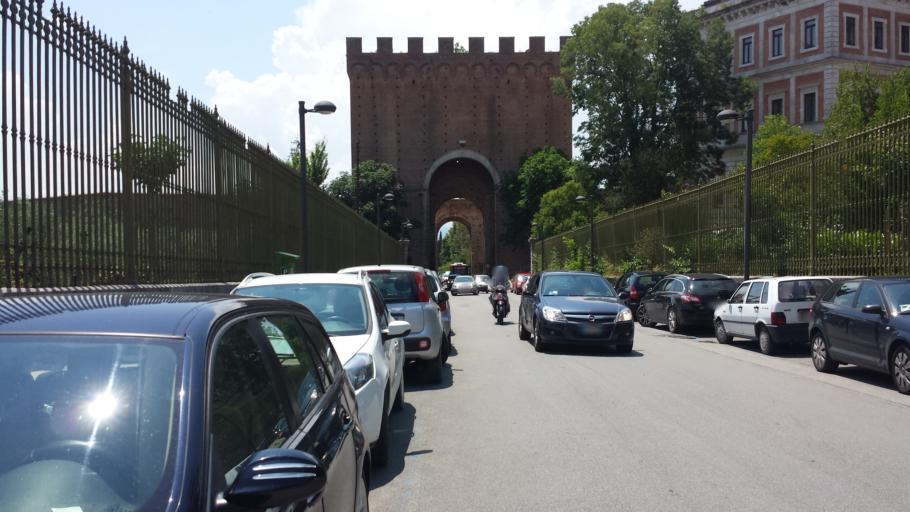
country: IT
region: Tuscany
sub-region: Provincia di Siena
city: Siena
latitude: 43.3143
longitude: 11.3396
